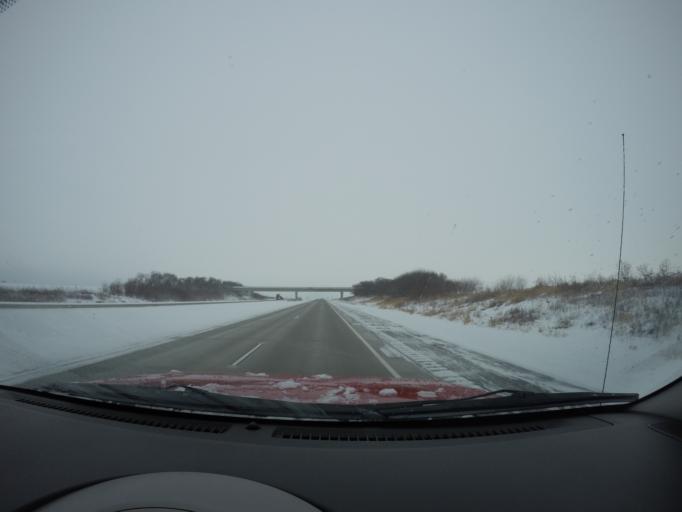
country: US
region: Minnesota
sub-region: Olmsted County
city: Eyota
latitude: 43.9554
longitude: -92.1774
